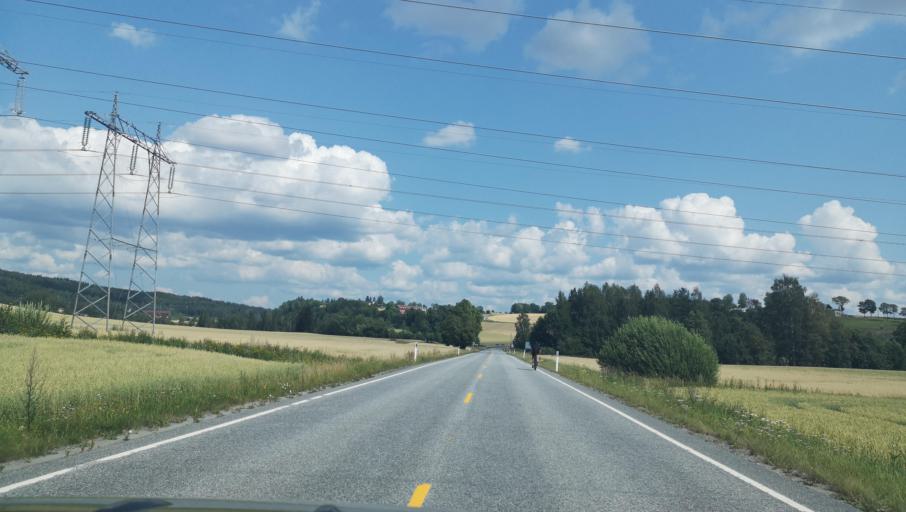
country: NO
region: Buskerud
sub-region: Ovre Eiker
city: Hokksund
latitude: 59.7233
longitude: 9.8308
